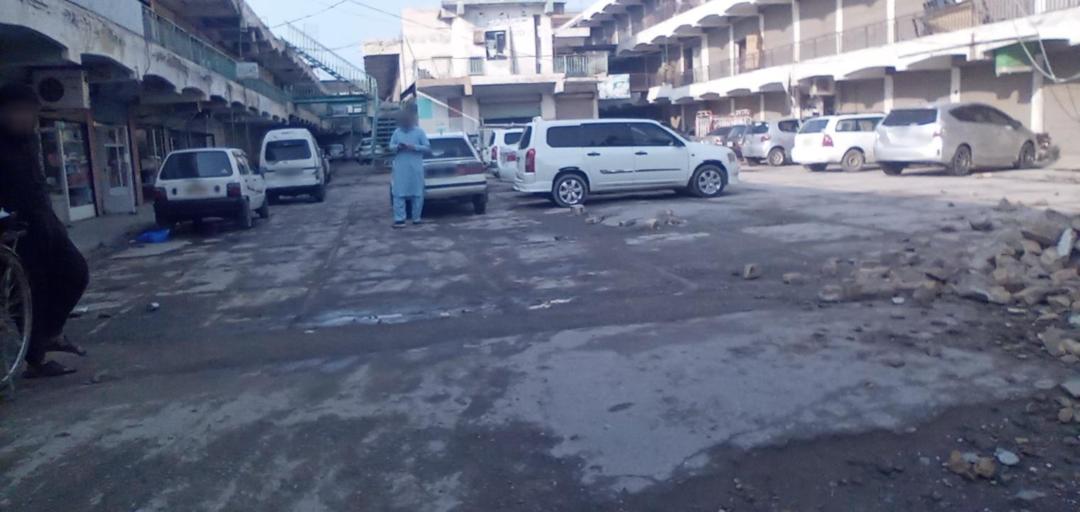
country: PK
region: Khyber Pakhtunkhwa
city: Peshawar
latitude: 33.9994
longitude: 71.4244
